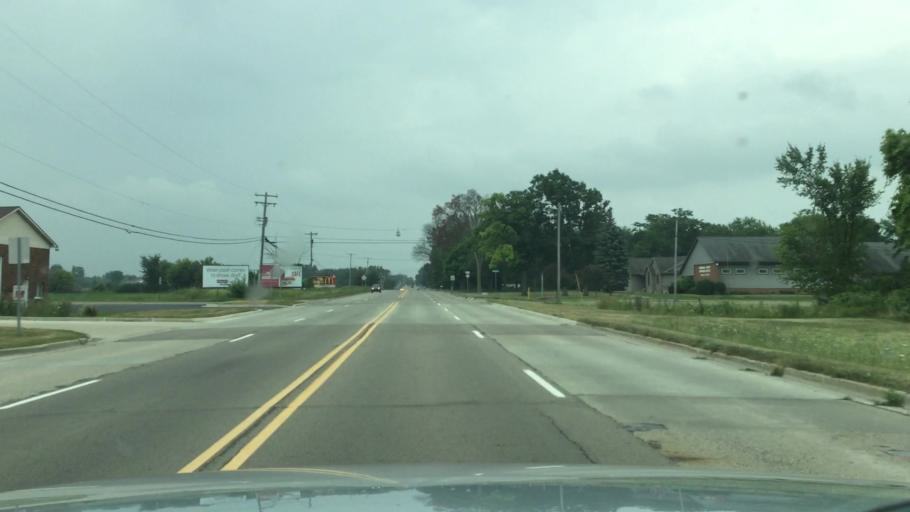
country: US
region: Michigan
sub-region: Shiawassee County
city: Owosso
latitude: 43.0274
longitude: -84.1769
